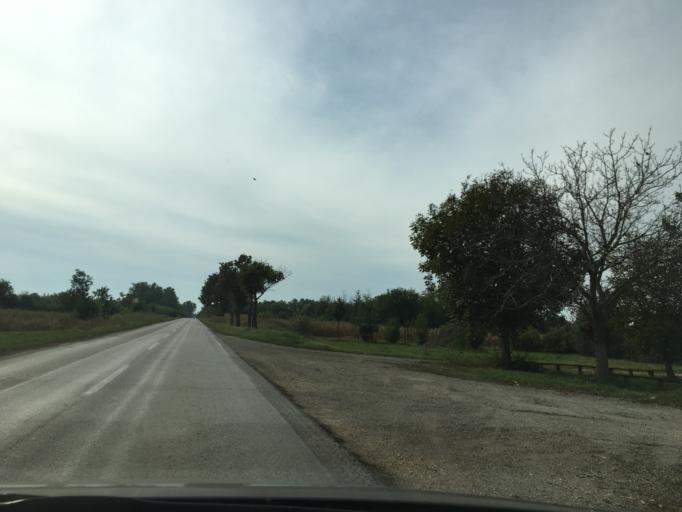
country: RS
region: Autonomna Pokrajina Vojvodina
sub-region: Juznobacki Okrug
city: Temerin
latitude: 45.4430
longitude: 19.9029
